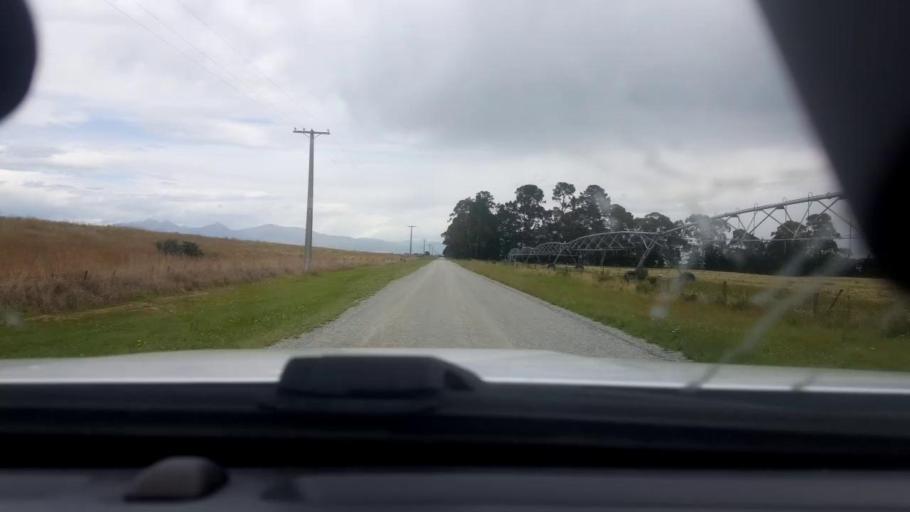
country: NZ
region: Canterbury
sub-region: Timaru District
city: Pleasant Point
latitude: -44.1529
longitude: 171.3965
